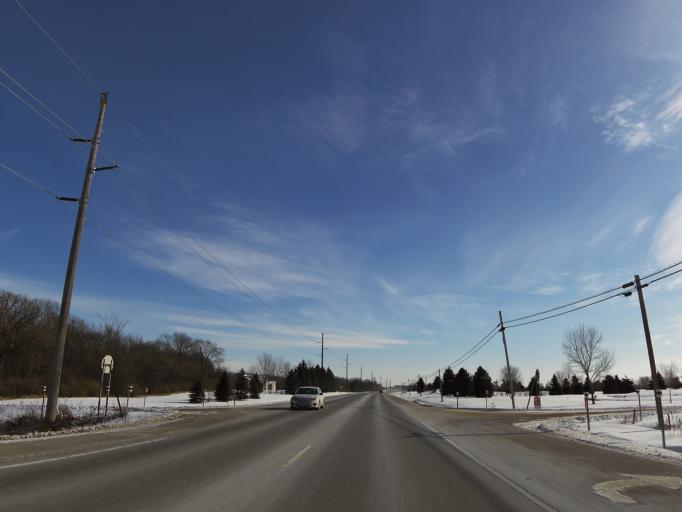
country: US
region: Minnesota
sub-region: Washington County
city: Cottage Grove
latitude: 44.7422
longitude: -92.9750
